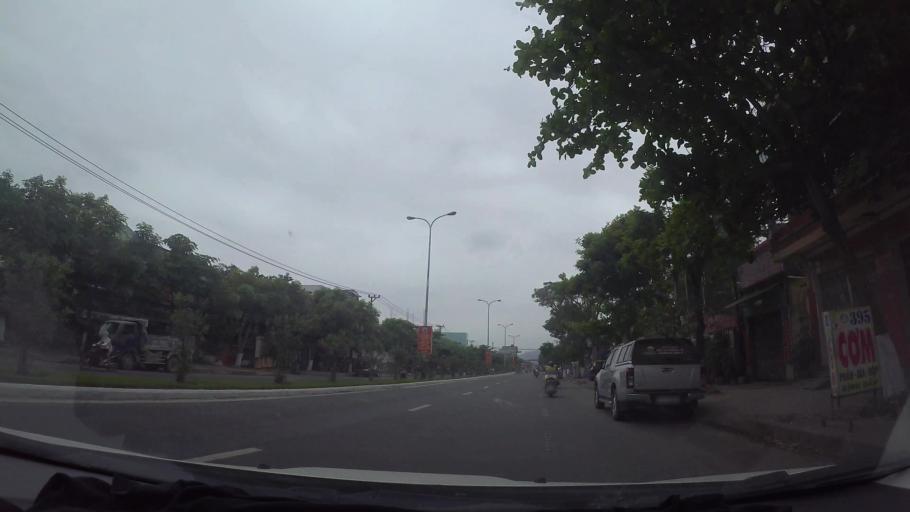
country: VN
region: Da Nang
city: Lien Chieu
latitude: 16.0855
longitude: 108.1448
